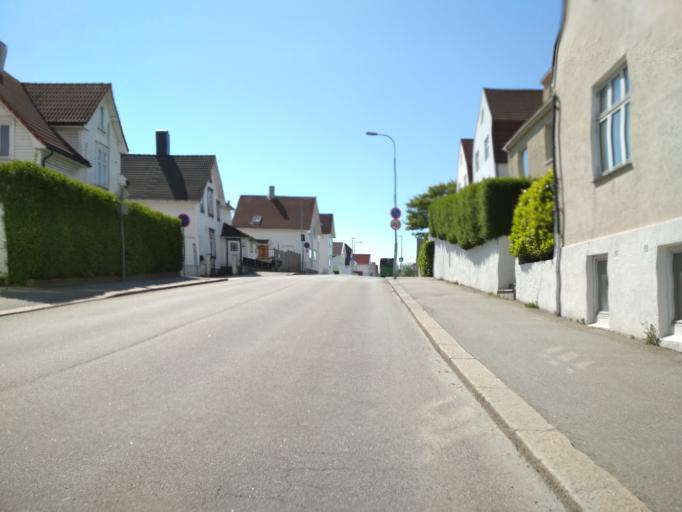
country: NO
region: Rogaland
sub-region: Stavanger
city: Stavanger
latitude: 58.9706
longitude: 5.7203
